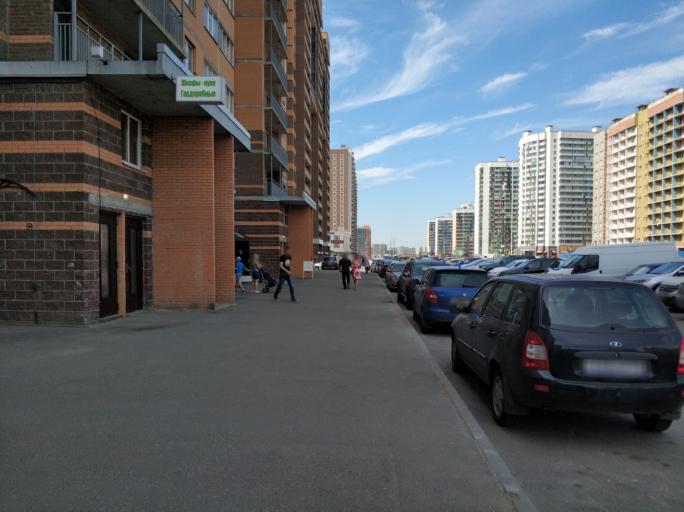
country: RU
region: Leningrad
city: Murino
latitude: 60.0568
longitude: 30.4330
